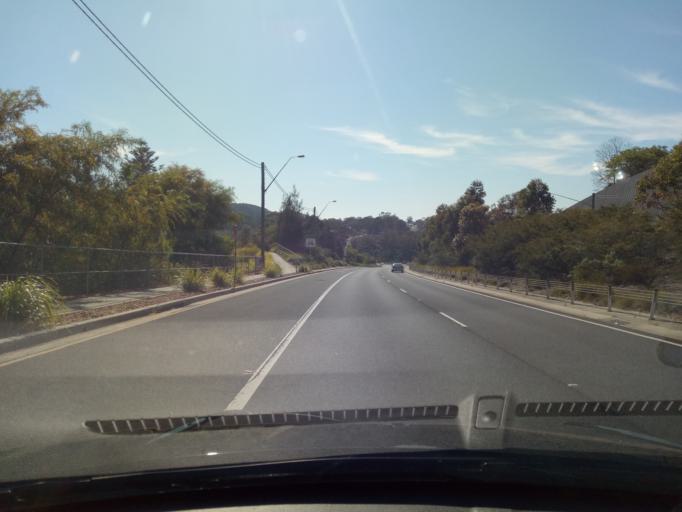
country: AU
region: New South Wales
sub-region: Gosford Shire
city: Holgate
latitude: -33.4260
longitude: 151.4219
